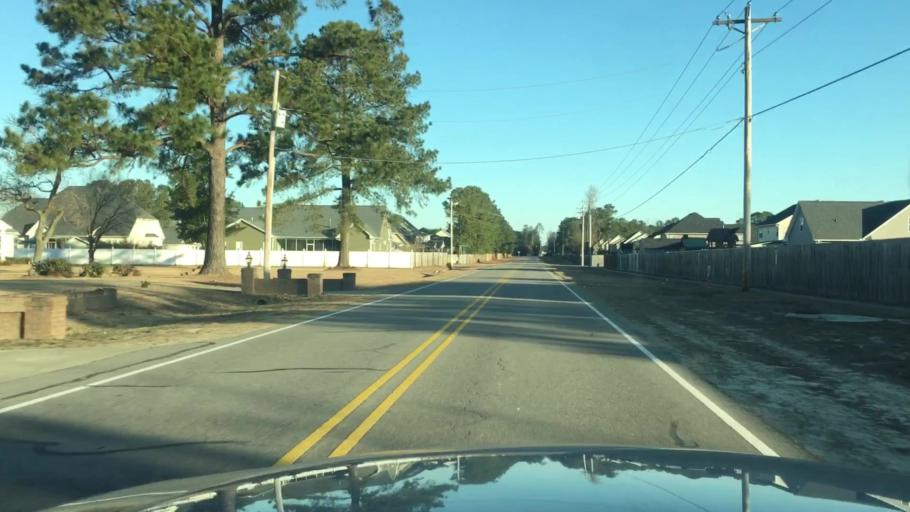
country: US
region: North Carolina
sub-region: Cumberland County
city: Hope Mills
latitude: 34.9685
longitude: -79.0079
